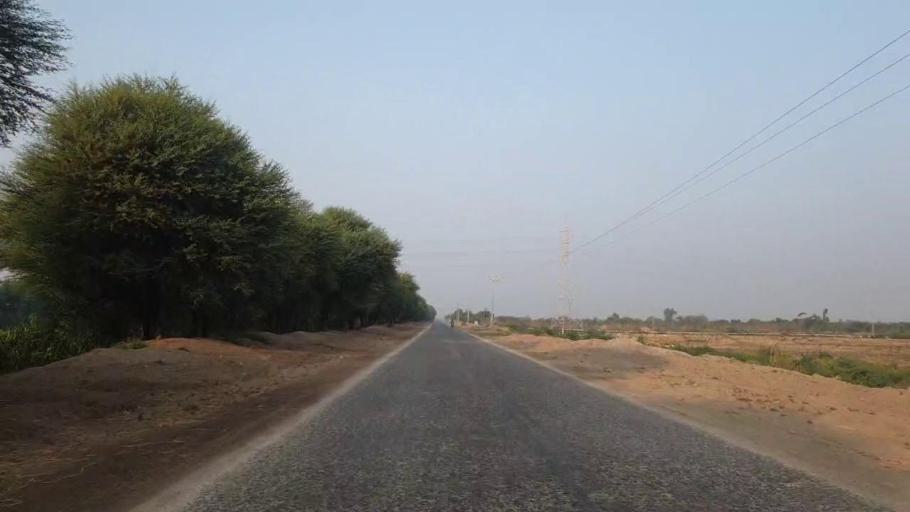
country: PK
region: Sindh
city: Tando Muhammad Khan
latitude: 25.1236
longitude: 68.4303
